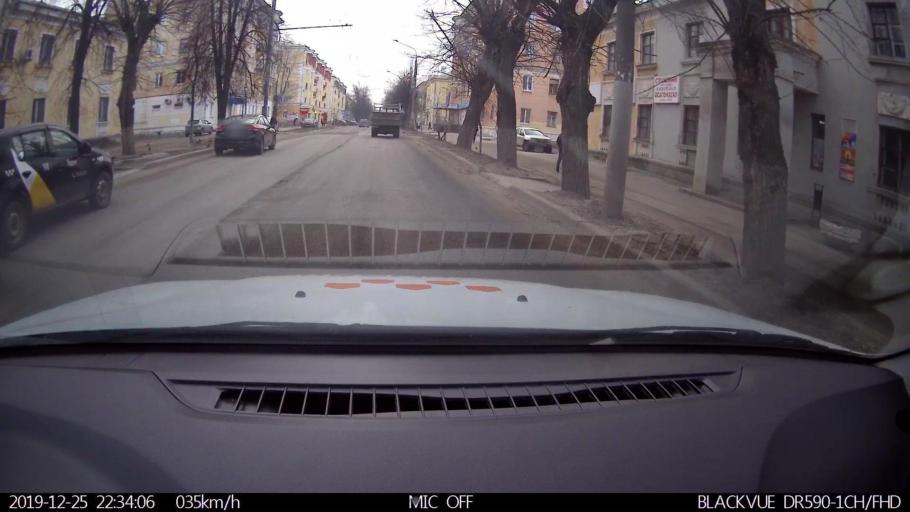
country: RU
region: Nizjnij Novgorod
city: Nizhniy Novgorod
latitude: 56.3339
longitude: 43.8808
